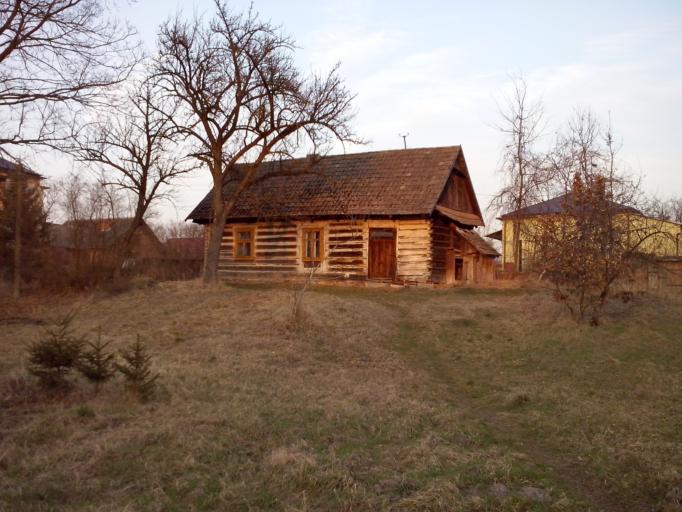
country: PL
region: Subcarpathian Voivodeship
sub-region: Powiat nizanski
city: Krzeszow
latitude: 50.3893
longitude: 22.3607
